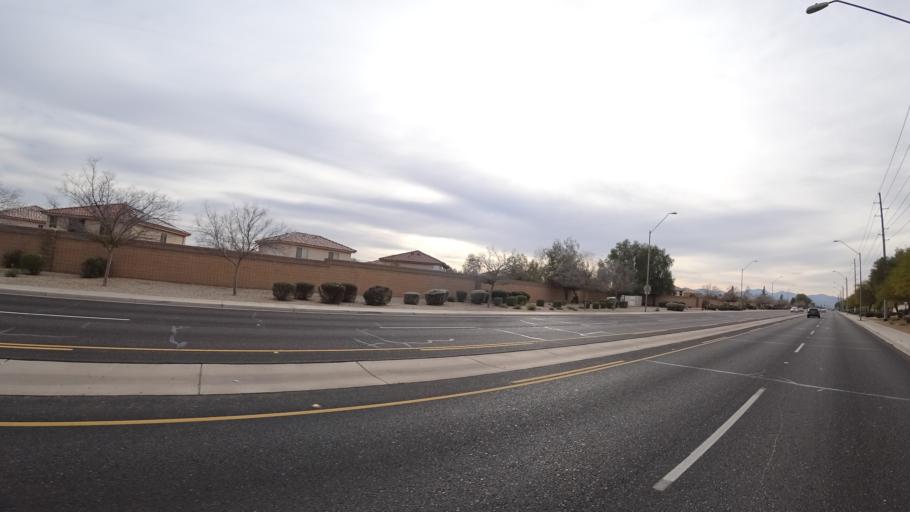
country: US
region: Arizona
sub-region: Maricopa County
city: El Mirage
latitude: 33.5946
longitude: -112.3348
